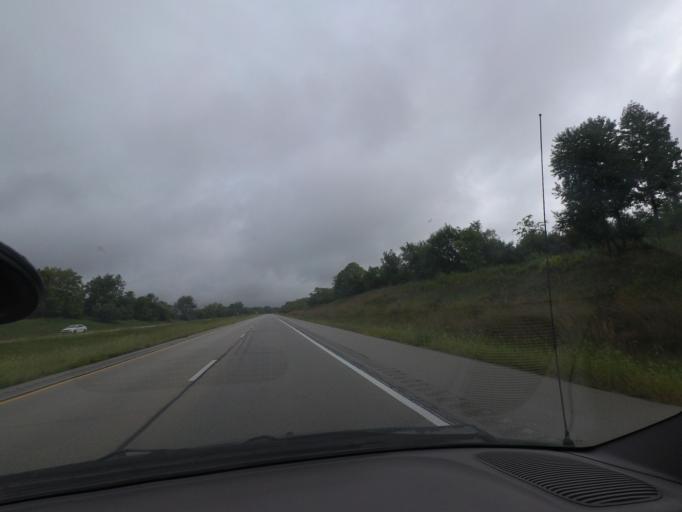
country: US
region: Illinois
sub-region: Piatt County
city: Monticello
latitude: 40.0659
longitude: -88.5485
